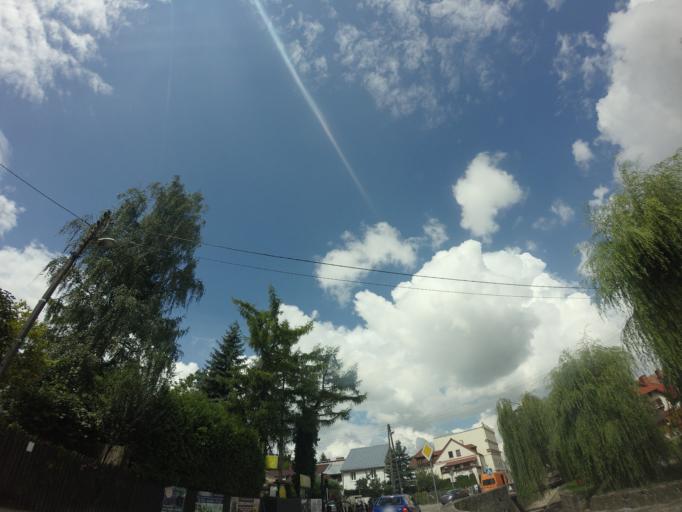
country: PL
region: Lublin Voivodeship
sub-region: Powiat pulawski
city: Kazimierz Dolny
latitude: 51.3210
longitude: 21.9472
